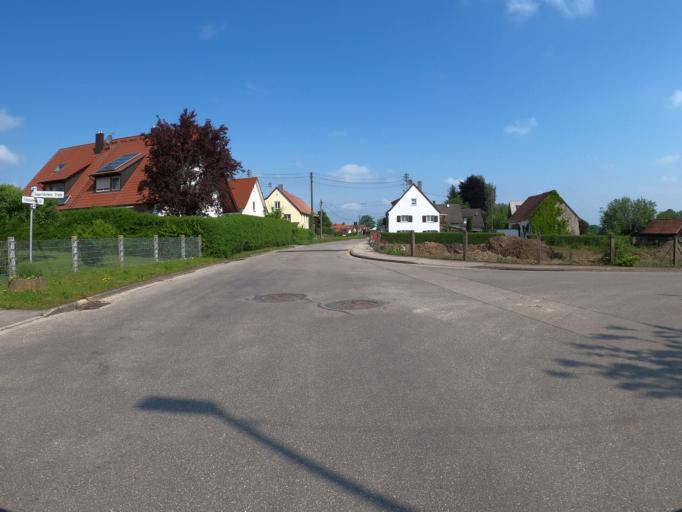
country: DE
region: Bavaria
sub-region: Swabia
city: Pfaffenhofen an der Roth
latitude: 48.3449
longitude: 10.1549
